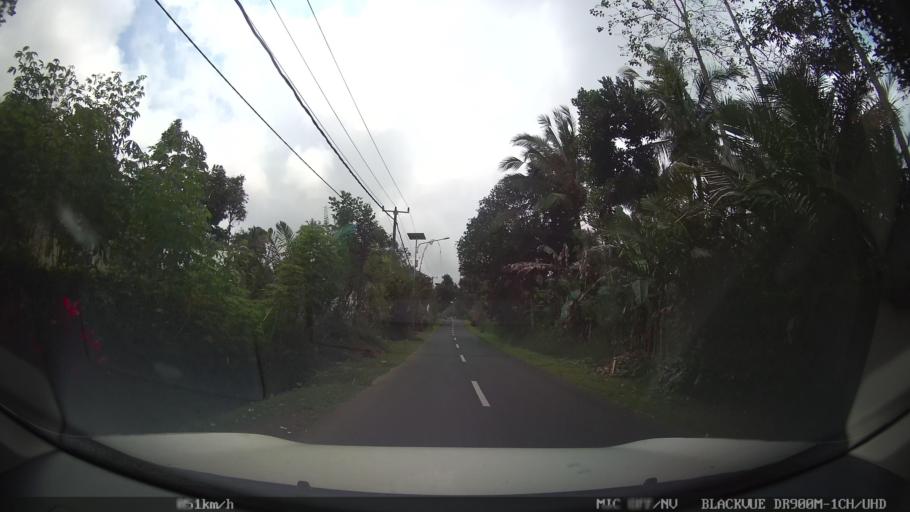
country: ID
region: Bali
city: Banjar Geriana Kangin
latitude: -8.4061
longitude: 115.4394
